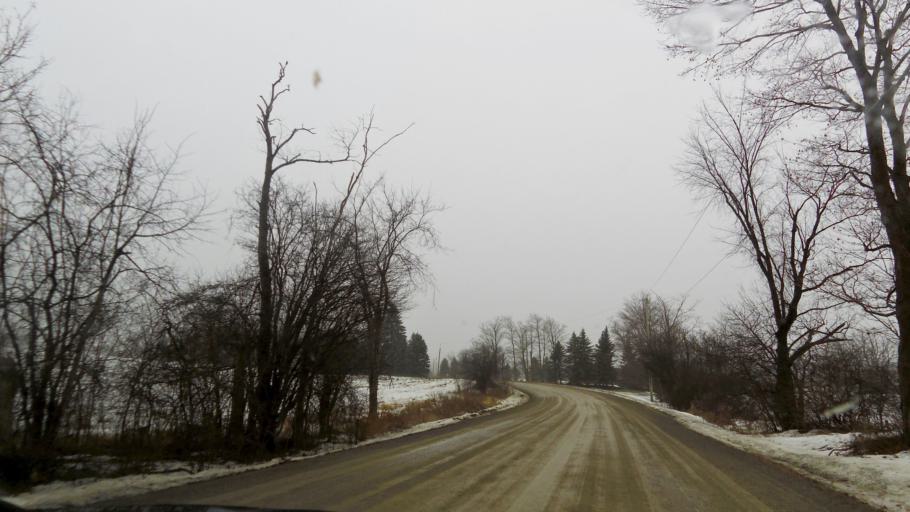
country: CA
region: Ontario
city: Brampton
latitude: 43.8381
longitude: -79.8569
